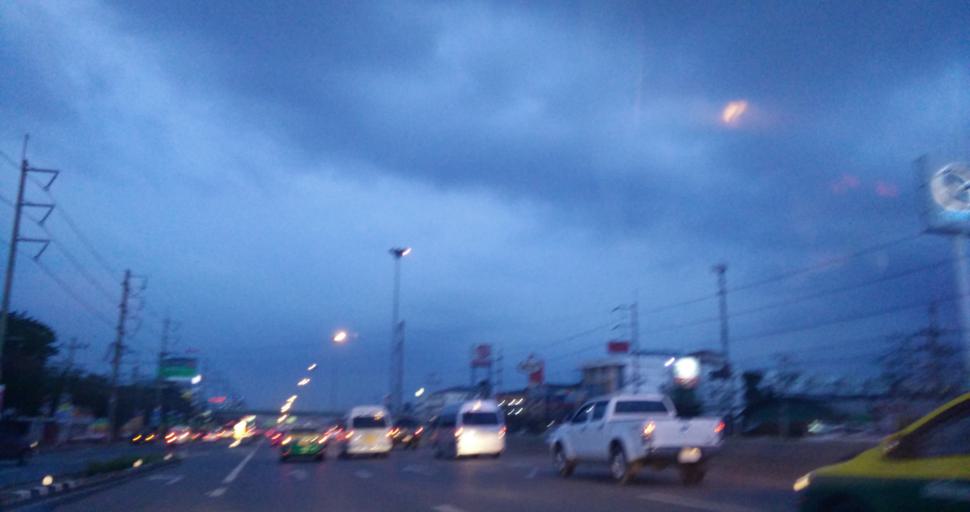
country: TH
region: Pathum Thani
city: Khlong Luang
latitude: 14.0168
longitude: 100.6154
